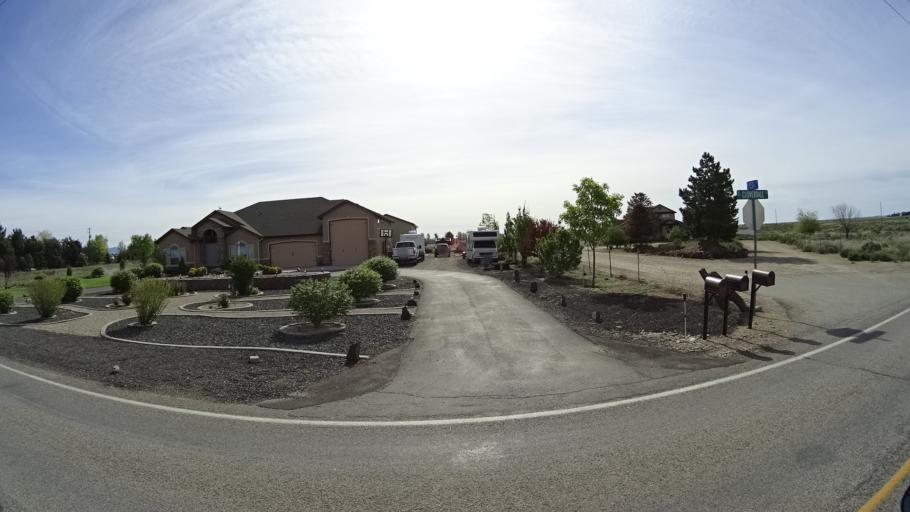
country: US
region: Idaho
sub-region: Ada County
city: Kuna
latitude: 43.4689
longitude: -116.3346
